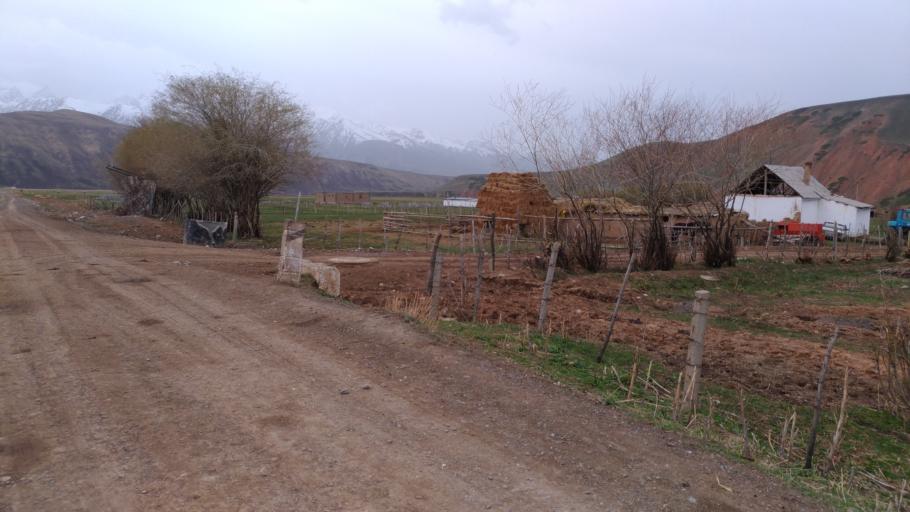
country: KG
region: Naryn
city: Naryn
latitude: 41.5146
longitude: 76.4399
